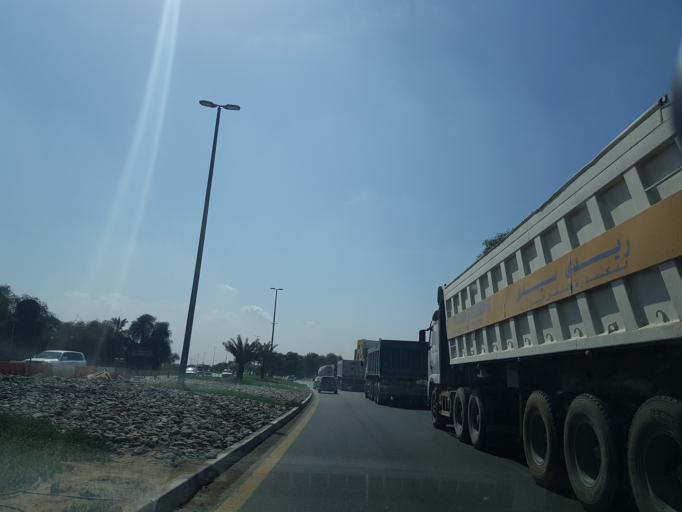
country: AE
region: Ra's al Khaymah
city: Ras al-Khaimah
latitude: 25.6986
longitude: 55.9670
